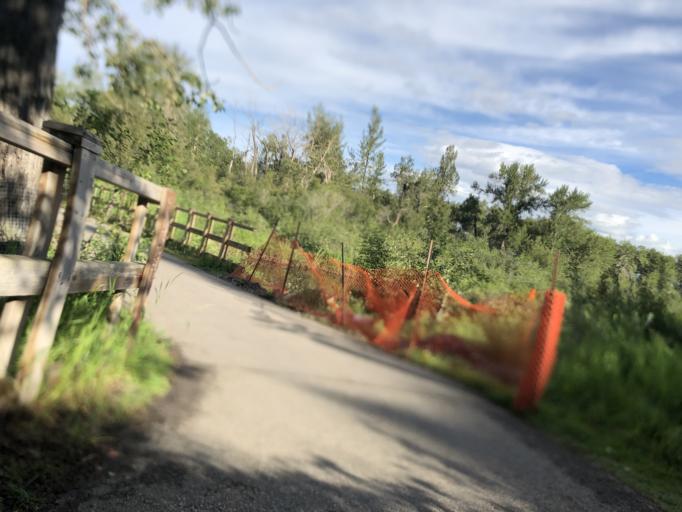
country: CA
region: Alberta
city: Calgary
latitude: 50.9990
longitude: -114.0232
